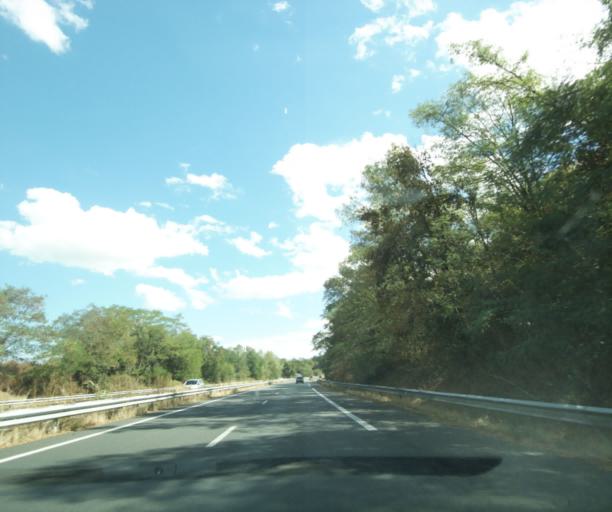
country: FR
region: Aquitaine
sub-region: Departement du Lot-et-Garonne
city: Meilhan-sur-Garonne
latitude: 44.4631
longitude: 0.0741
